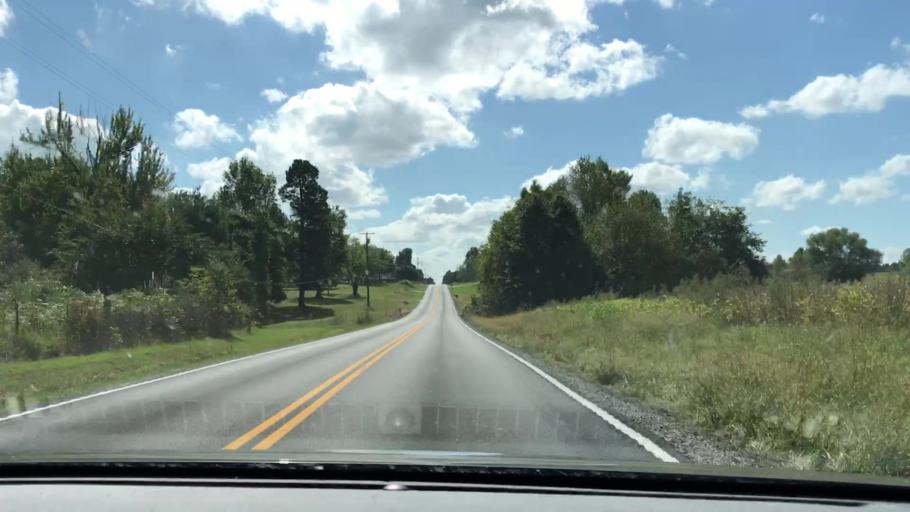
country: US
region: Kentucky
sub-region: Graves County
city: Mayfield
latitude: 36.8065
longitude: -88.5953
